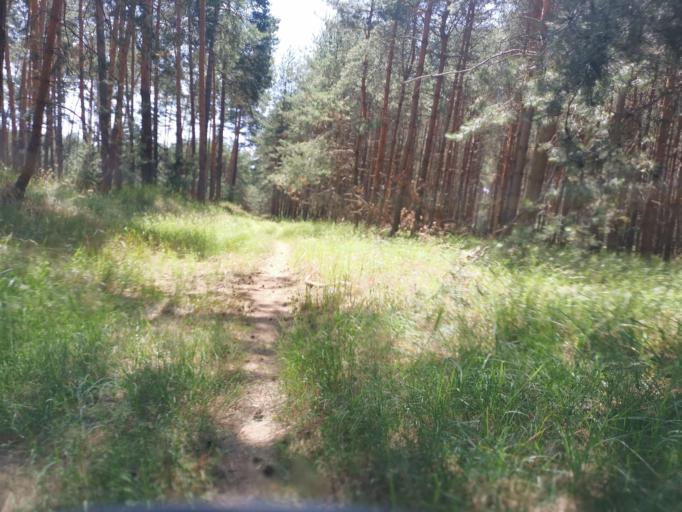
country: CZ
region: South Moravian
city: Petrov
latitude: 48.9230
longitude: 17.2432
